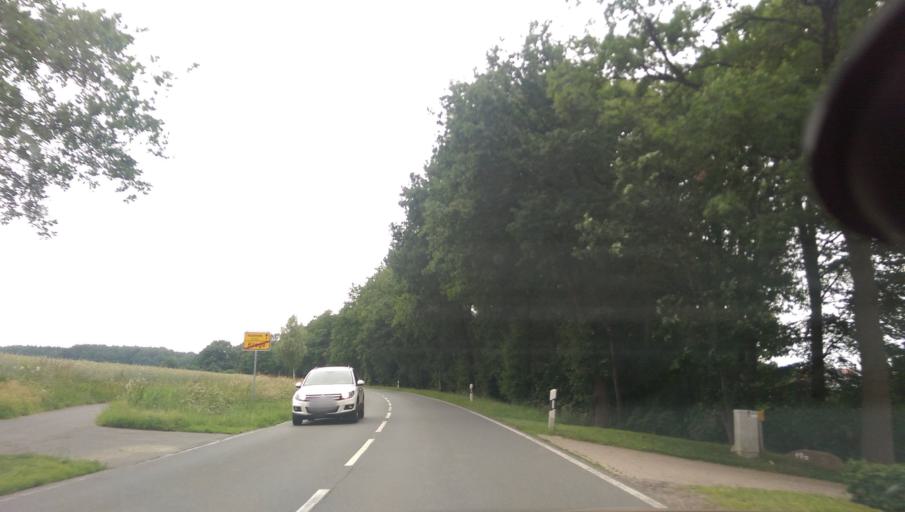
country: DE
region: Lower Saxony
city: Bomlitz
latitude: 52.9293
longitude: 9.6917
